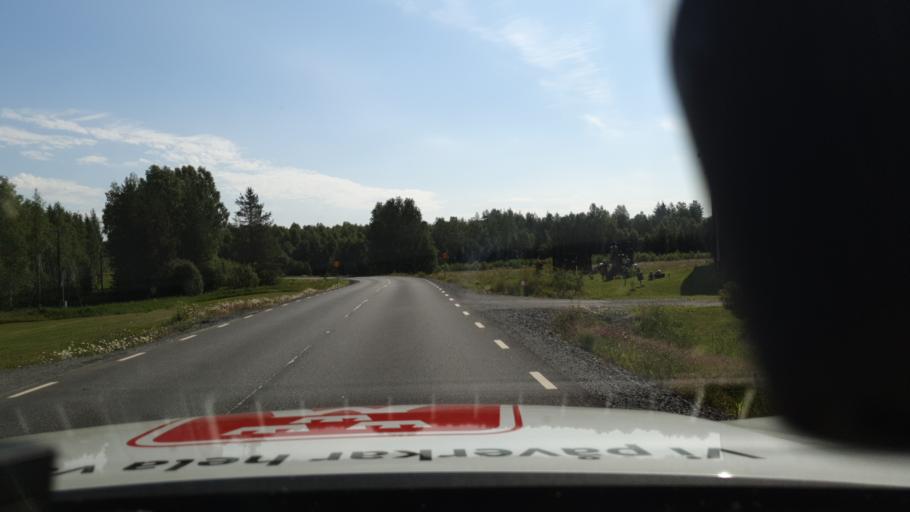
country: SE
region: Norrbotten
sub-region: Bodens Kommun
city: Saevast
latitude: 65.8356
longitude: 21.8473
